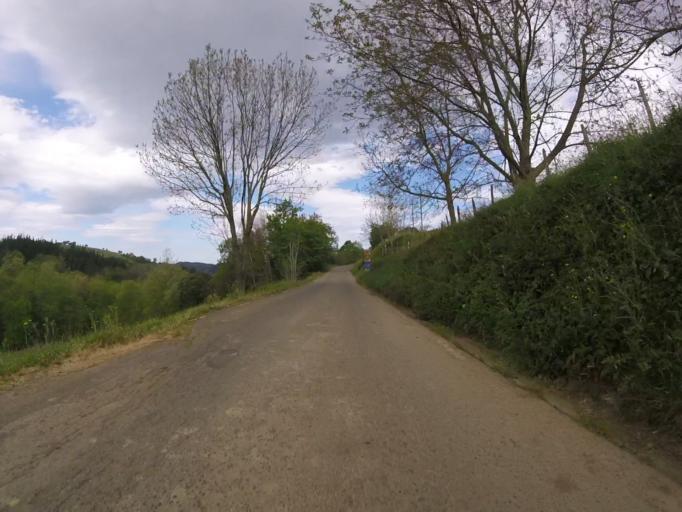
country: ES
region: Basque Country
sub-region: Provincia de Guipuzcoa
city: Zarautz
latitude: 43.2610
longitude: -2.1681
